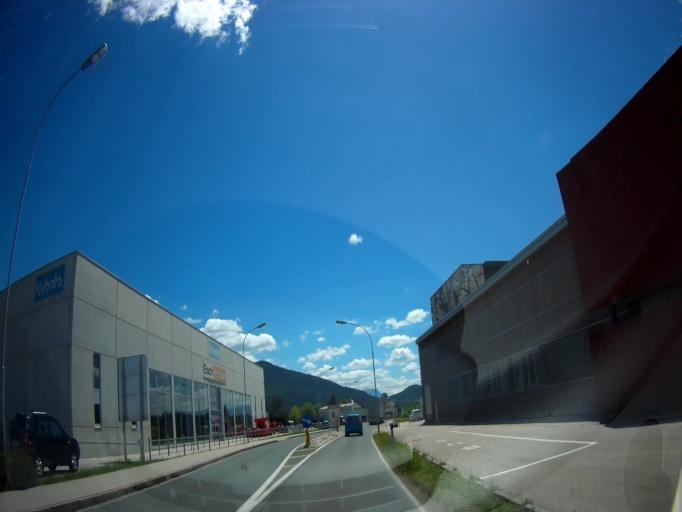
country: AT
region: Carinthia
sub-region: Politischer Bezirk Sankt Veit an der Glan
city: Sankt Veit an der Glan
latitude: 46.7535
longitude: 14.3797
